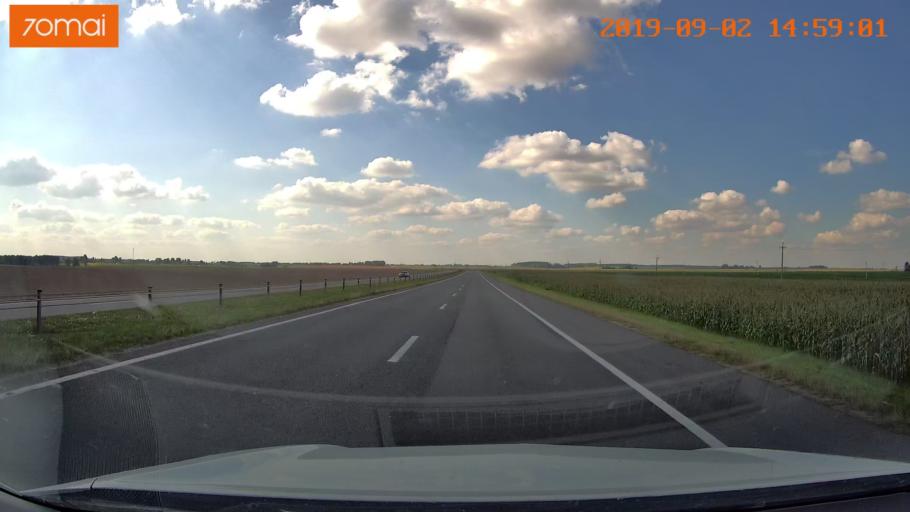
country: BY
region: Mogilev
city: Vishow
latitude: 53.9758
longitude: 30.1211
